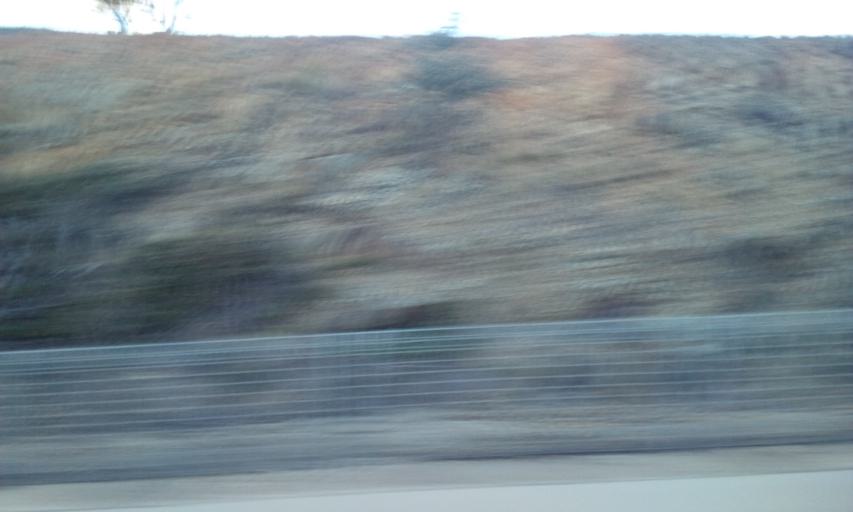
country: AU
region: New South Wales
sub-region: Yass Valley
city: Gundaroo
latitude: -35.1187
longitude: 149.3492
